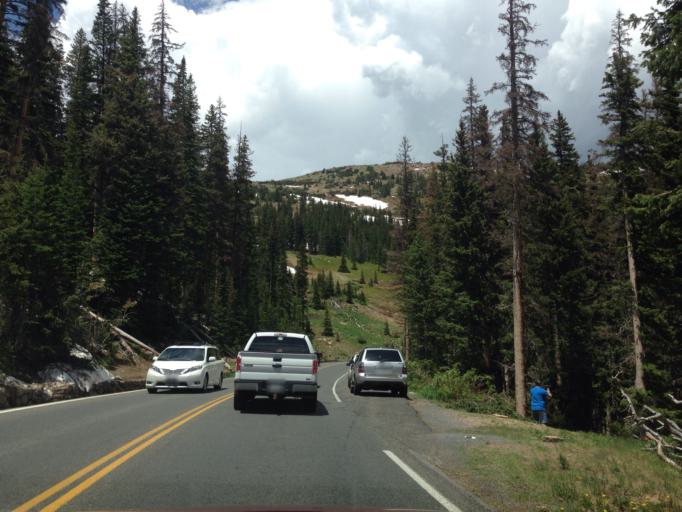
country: US
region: Colorado
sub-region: Larimer County
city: Estes Park
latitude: 40.3885
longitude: -105.6737
